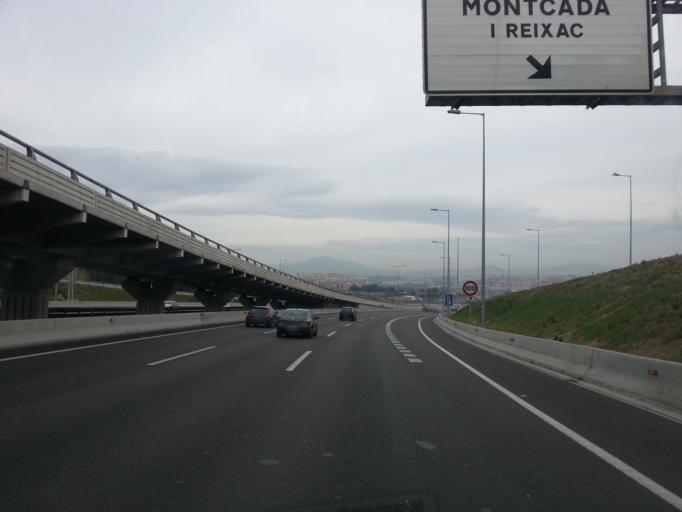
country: ES
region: Catalonia
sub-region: Provincia de Barcelona
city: Ripollet
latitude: 41.4799
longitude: 2.1611
